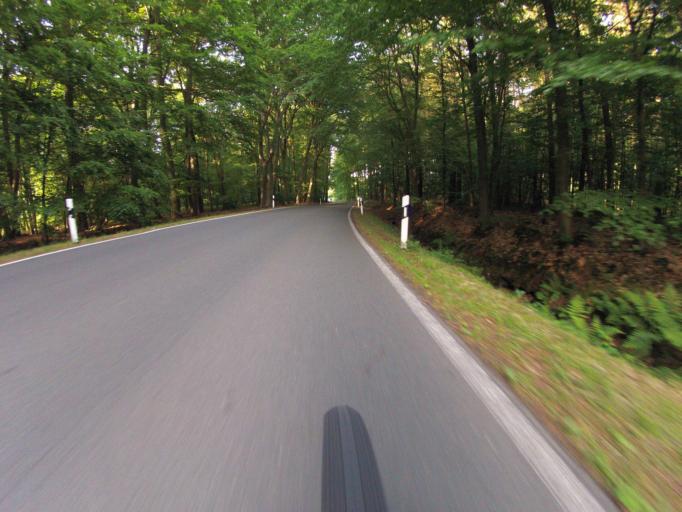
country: DE
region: North Rhine-Westphalia
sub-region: Regierungsbezirk Munster
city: Birgte
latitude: 52.2666
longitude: 7.6746
